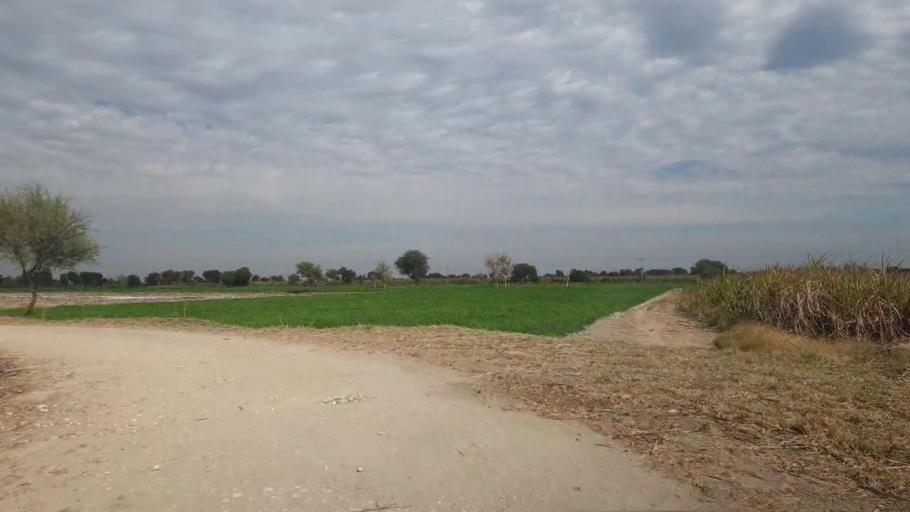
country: PK
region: Sindh
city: Jhol
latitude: 26.0153
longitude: 68.8758
